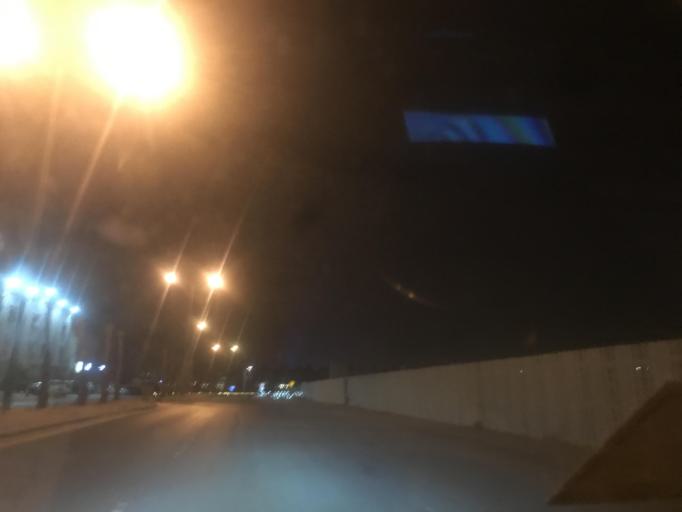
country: SA
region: Ar Riyad
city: Riyadh
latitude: 24.8001
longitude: 46.5936
